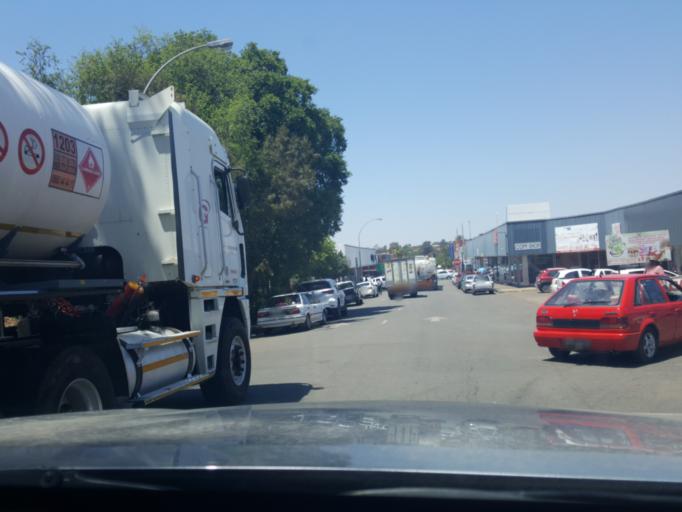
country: ZA
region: North-West
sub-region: Ngaka Modiri Molema District Municipality
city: Zeerust
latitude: -25.5438
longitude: 26.0797
